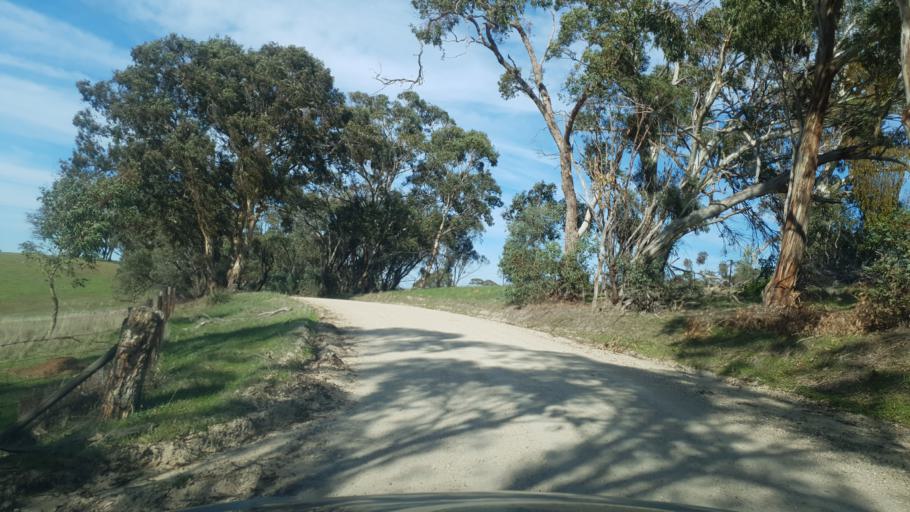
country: AU
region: South Australia
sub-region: Playford
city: One Tree Hill
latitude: -34.6502
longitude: 138.8089
